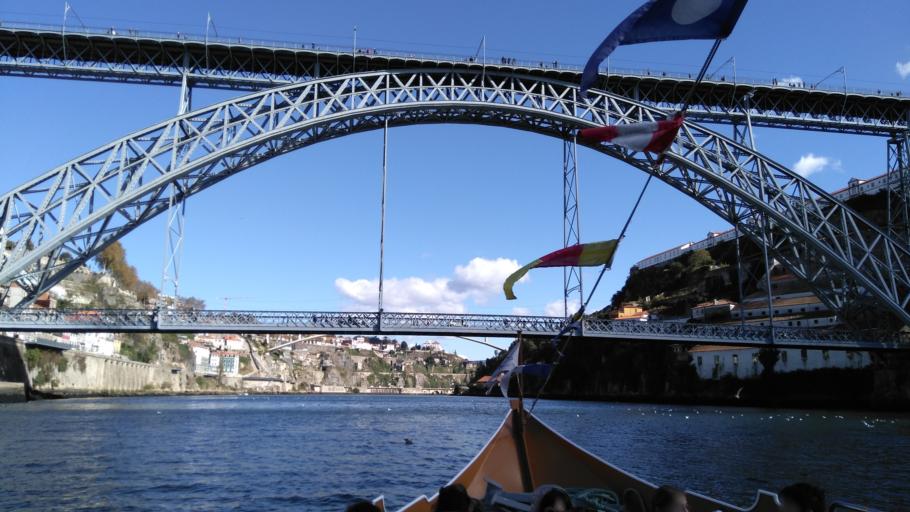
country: PT
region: Porto
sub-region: Vila Nova de Gaia
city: Vila Nova de Gaia
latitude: 41.1399
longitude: -8.6110
